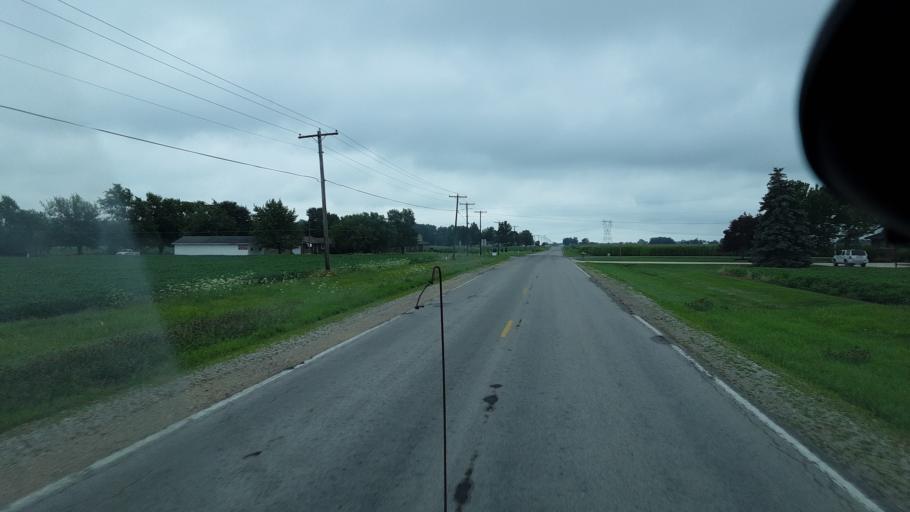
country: US
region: Indiana
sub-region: Wells County
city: Bluffton
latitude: 40.7729
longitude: -85.0905
